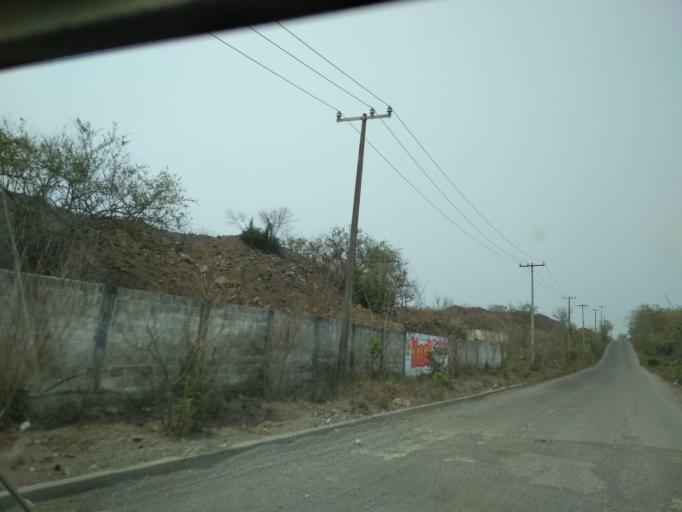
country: MX
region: Veracruz
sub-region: Veracruz
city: Delfino Victoria (Santa Fe)
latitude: 19.1854
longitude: -96.3177
